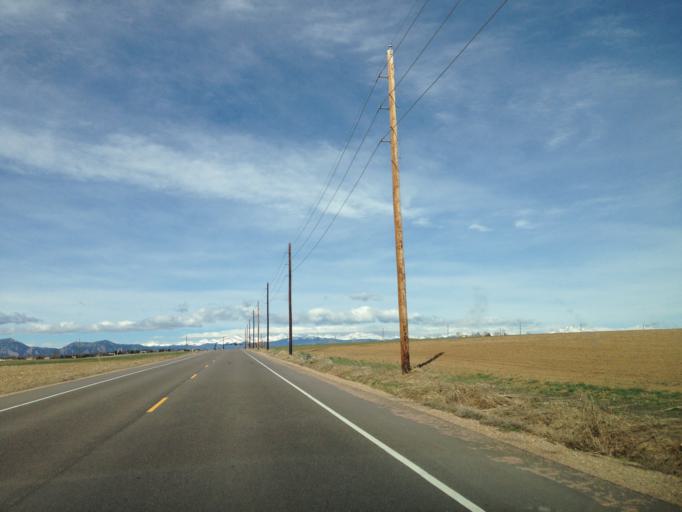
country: US
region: Colorado
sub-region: Boulder County
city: Lafayette
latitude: 40.0149
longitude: -105.0681
